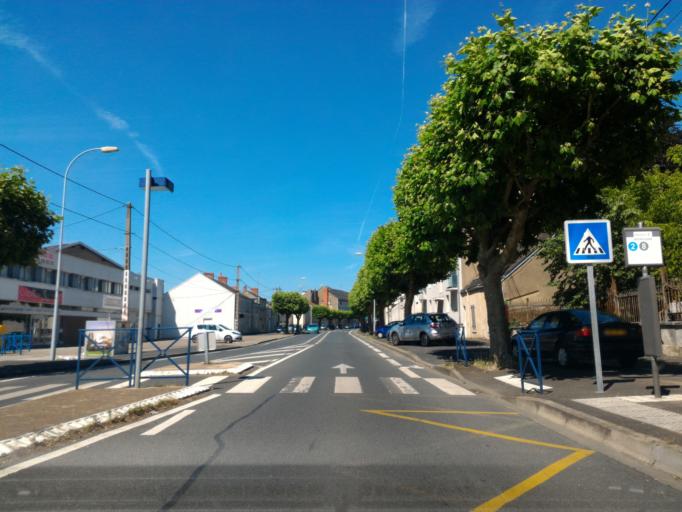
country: FR
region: Centre
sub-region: Departement de l'Indre
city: Chateauroux
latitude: 46.8060
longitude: 1.6752
